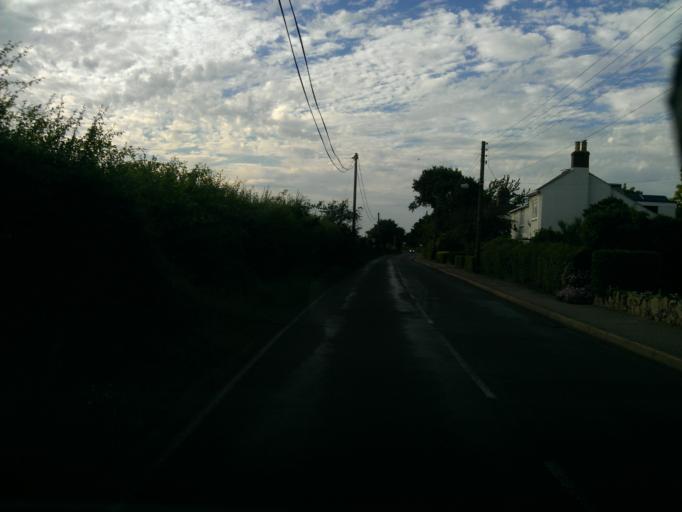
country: GB
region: England
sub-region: Essex
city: Great Bentley
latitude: 51.8428
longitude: 1.0690
